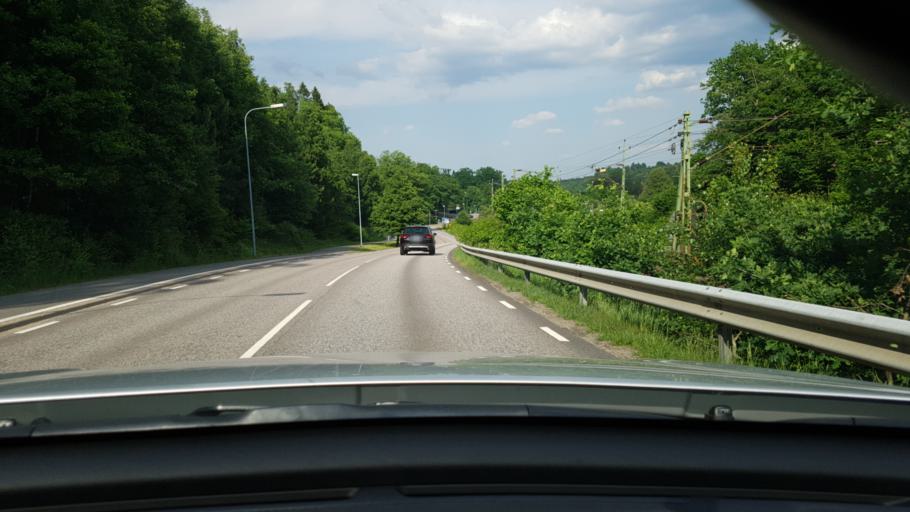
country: SE
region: Vaestra Goetaland
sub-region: Lerums Kommun
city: Stenkullen
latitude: 57.8064
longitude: 12.3520
